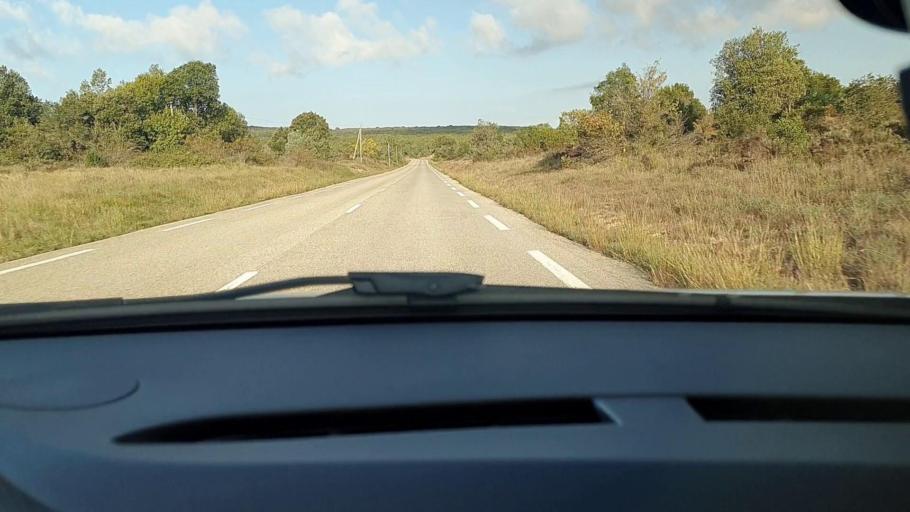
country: FR
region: Languedoc-Roussillon
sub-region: Departement du Gard
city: Barjac
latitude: 44.2144
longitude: 4.3326
